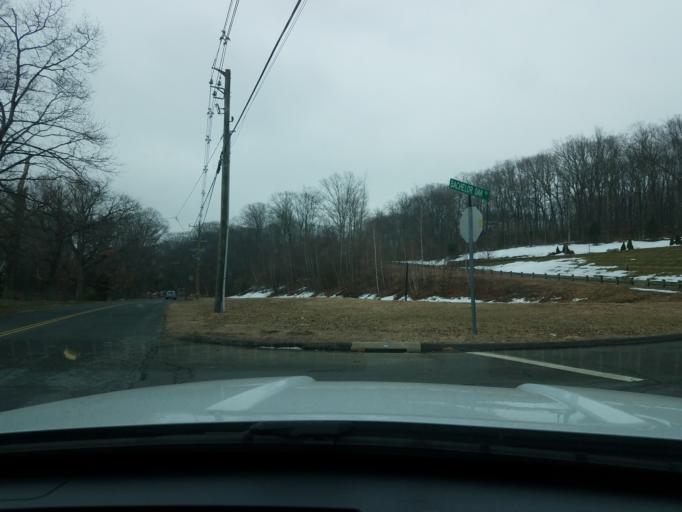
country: US
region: Connecticut
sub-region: New Haven County
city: Naugatuck
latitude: 41.4346
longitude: -73.0244
